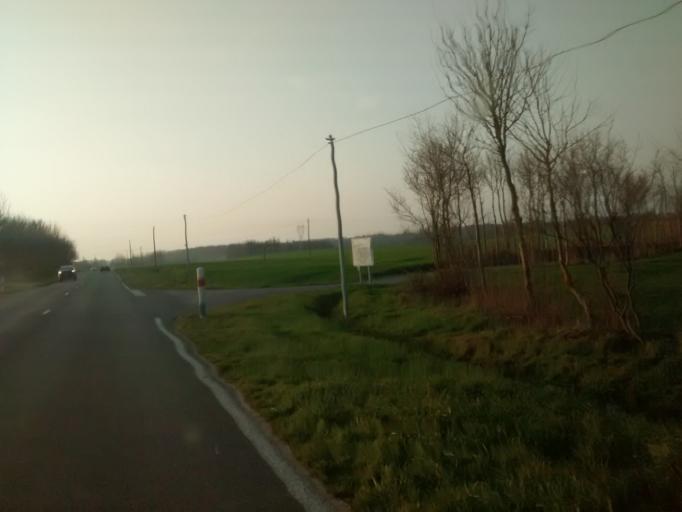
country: FR
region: Brittany
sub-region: Departement d'Ille-et-Vilaine
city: Chavagne
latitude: 48.0625
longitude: -1.8099
